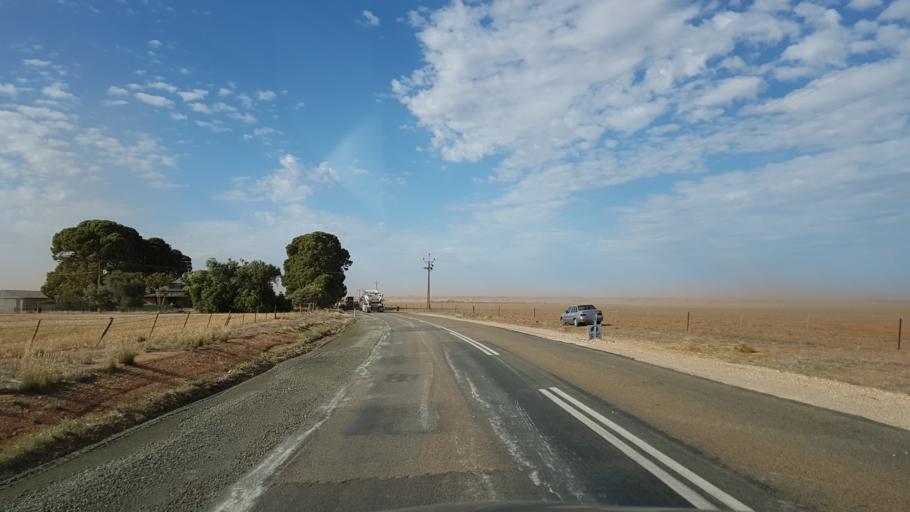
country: AU
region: South Australia
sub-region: Clare and Gilbert Valleys
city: Clare
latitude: -33.8802
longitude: 138.4791
